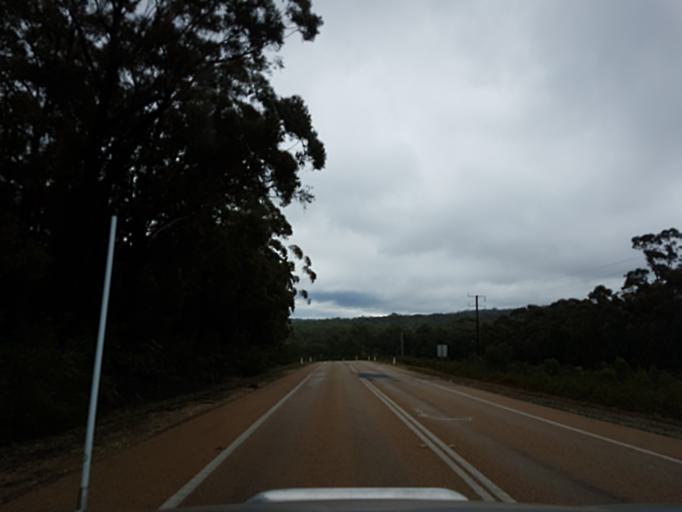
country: AU
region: Victoria
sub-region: East Gippsland
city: Lakes Entrance
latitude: -37.6904
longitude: 148.0132
